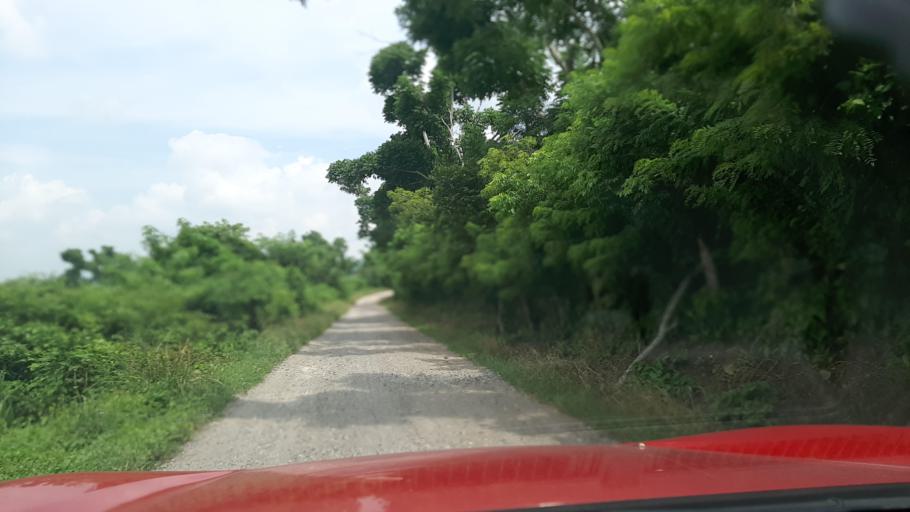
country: MX
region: Veracruz
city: Gutierrez Zamora
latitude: 20.4562
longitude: -97.1781
